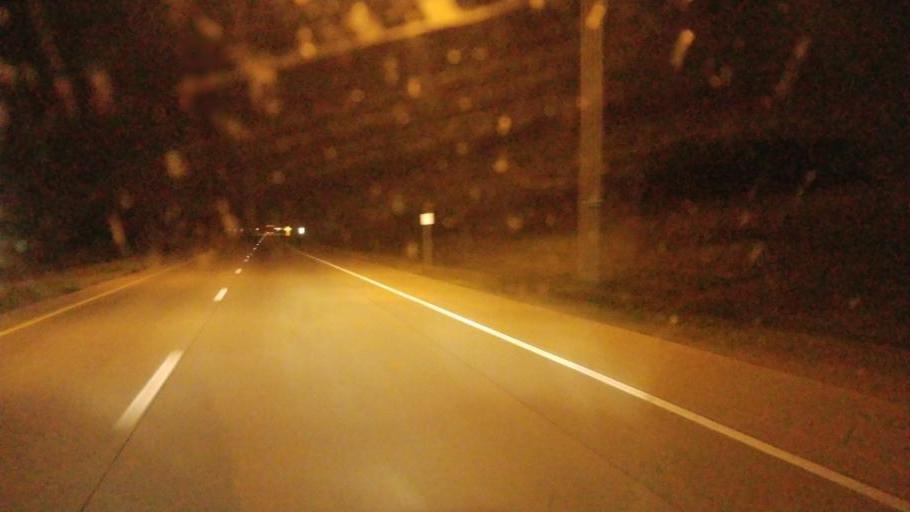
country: US
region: Ohio
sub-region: Hardin County
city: Ada
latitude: 40.8276
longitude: -83.8344
